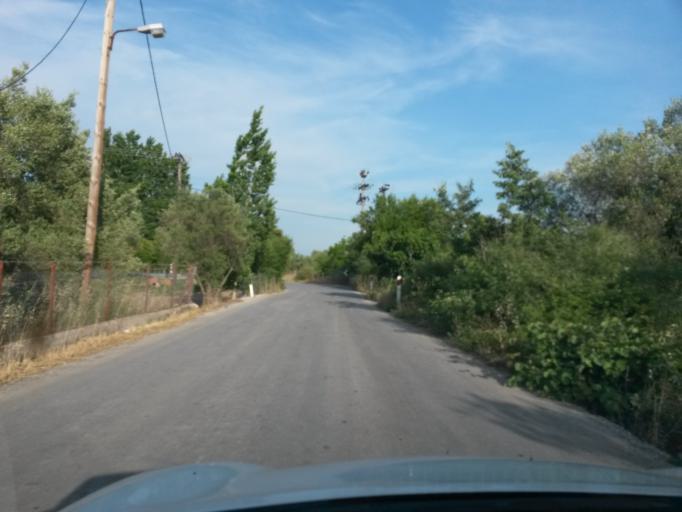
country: GR
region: North Aegean
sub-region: Nomos Lesvou
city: Kalloni
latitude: 39.2404
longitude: 26.2056
